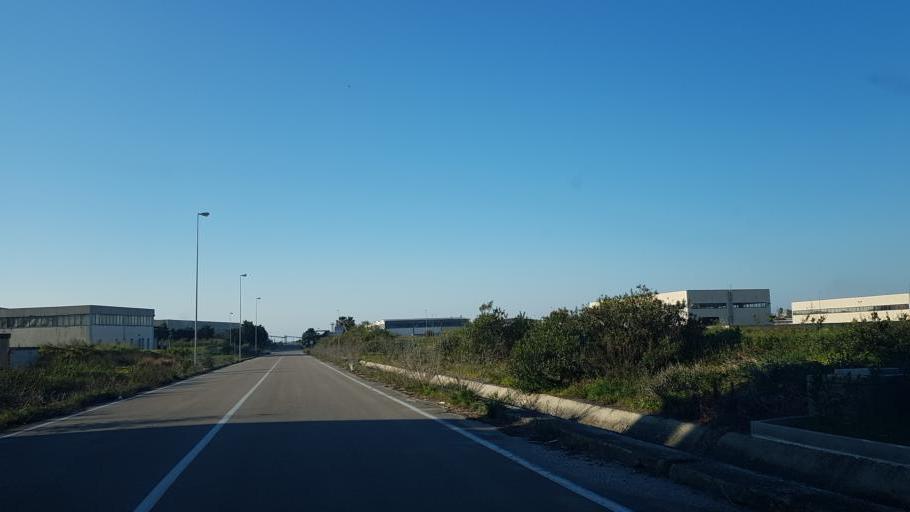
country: IT
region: Apulia
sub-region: Provincia di Brindisi
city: La Rosa
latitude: 40.6237
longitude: 17.9710
